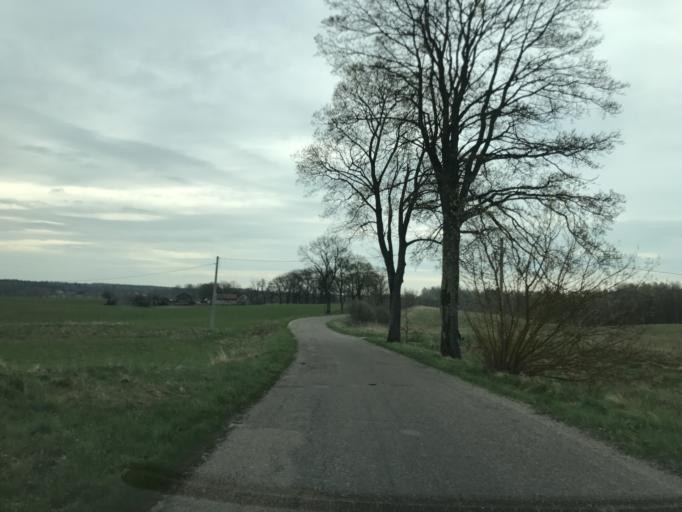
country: PL
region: Warmian-Masurian Voivodeship
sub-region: Powiat olsztynski
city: Olsztynek
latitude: 53.6308
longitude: 20.2028
